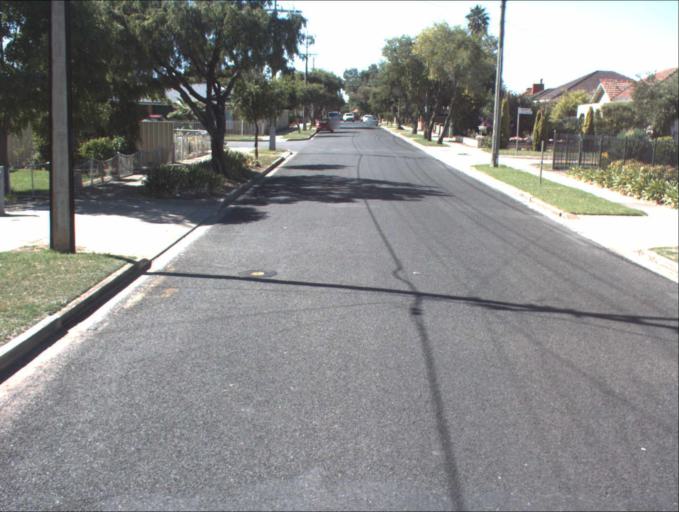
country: AU
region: South Australia
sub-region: Port Adelaide Enfield
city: Blair Athol
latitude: -34.8717
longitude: 138.6132
